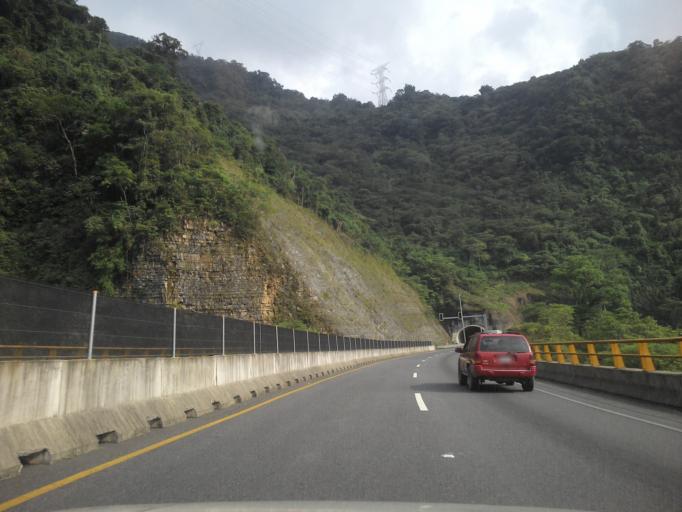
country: MX
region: Puebla
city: Xicotepec de Juarez
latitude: 20.3182
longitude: -97.9638
